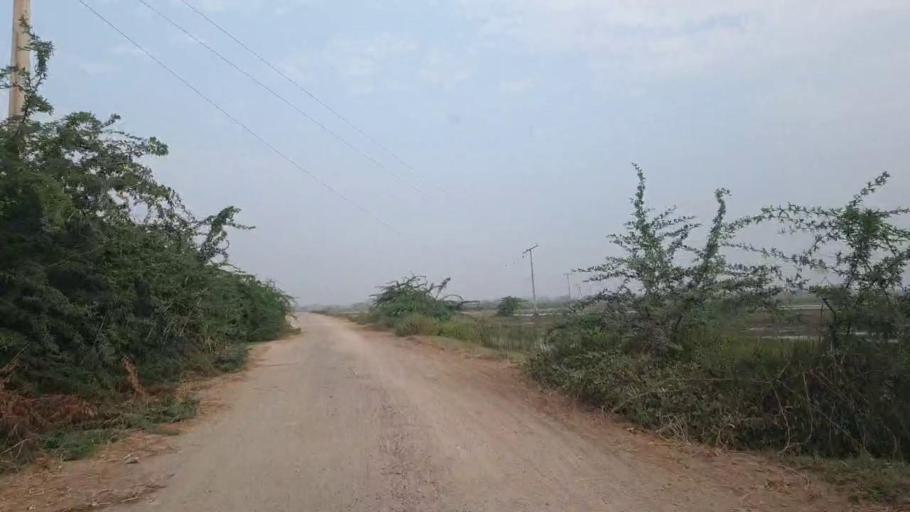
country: PK
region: Sindh
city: Tando Bago
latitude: 24.7845
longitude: 68.8874
